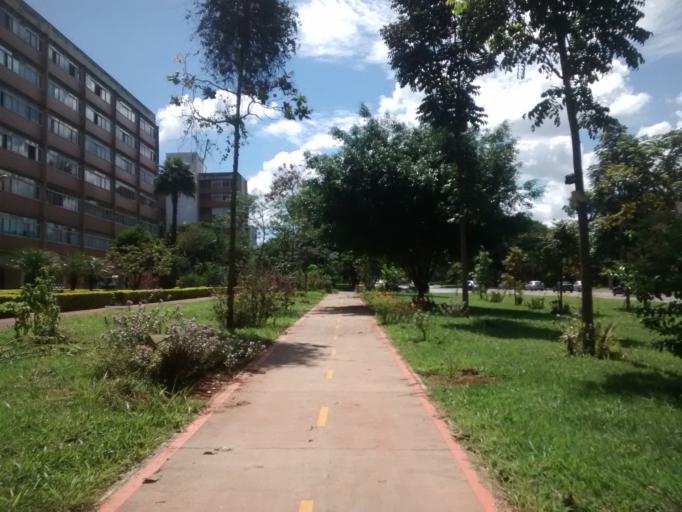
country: BR
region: Federal District
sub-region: Brasilia
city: Brasilia
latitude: -15.7793
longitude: -47.8845
